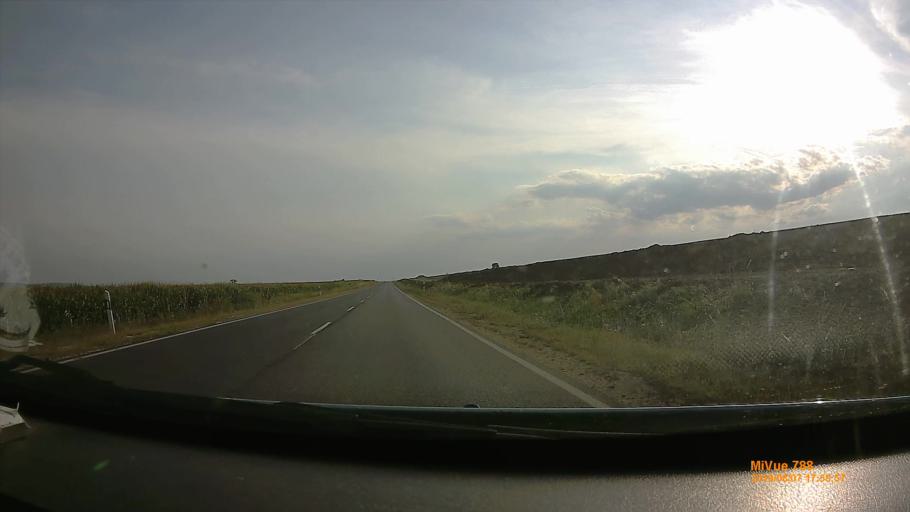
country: HU
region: Borsod-Abauj-Zemplen
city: Encs
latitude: 48.3103
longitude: 21.0737
